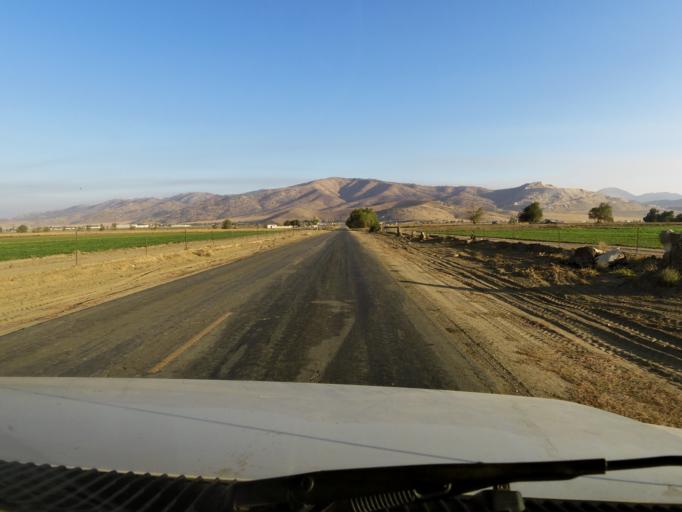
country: US
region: California
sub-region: Kern County
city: Tehachapi
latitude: 35.1115
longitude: -118.4145
